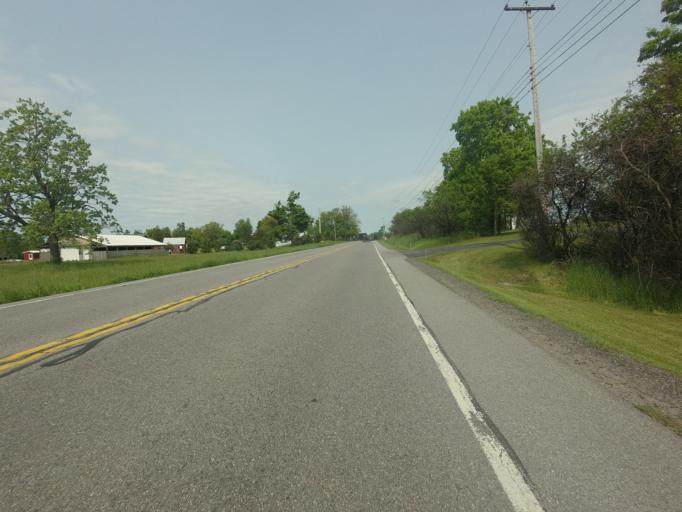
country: US
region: New York
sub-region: Jefferson County
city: Brownville
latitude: 44.0027
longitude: -76.0028
